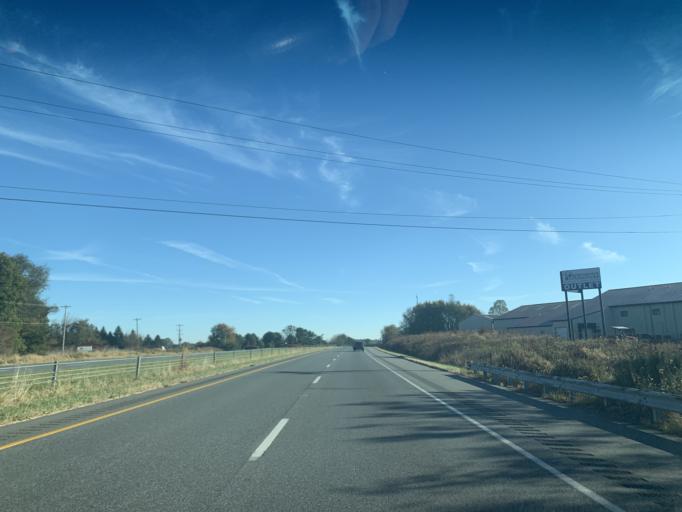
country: US
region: Pennsylvania
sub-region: Chester County
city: Oxford
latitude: 39.8050
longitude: -75.9717
